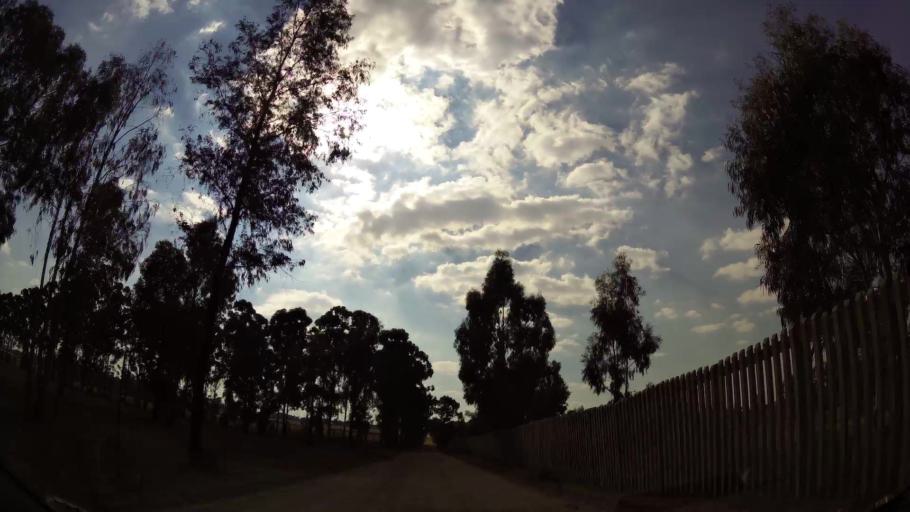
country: ZA
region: Gauteng
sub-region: Ekurhuleni Metropolitan Municipality
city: Benoni
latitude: -26.0866
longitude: 28.3670
